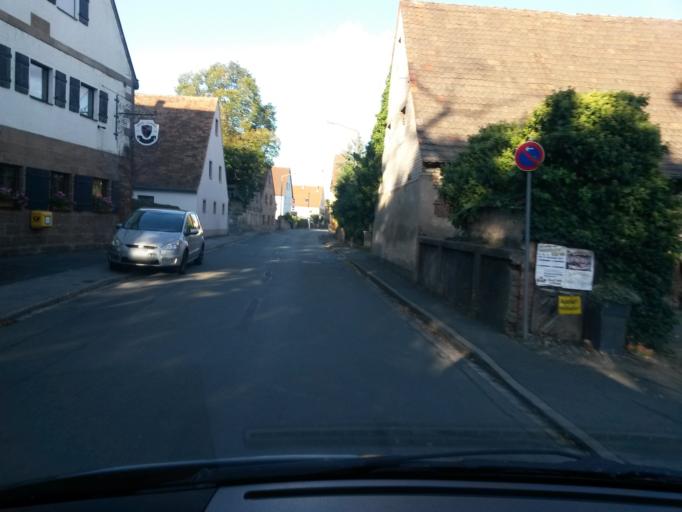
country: DE
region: Bavaria
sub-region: Regierungsbezirk Mittelfranken
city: Erlangen
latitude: 49.5333
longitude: 11.0225
